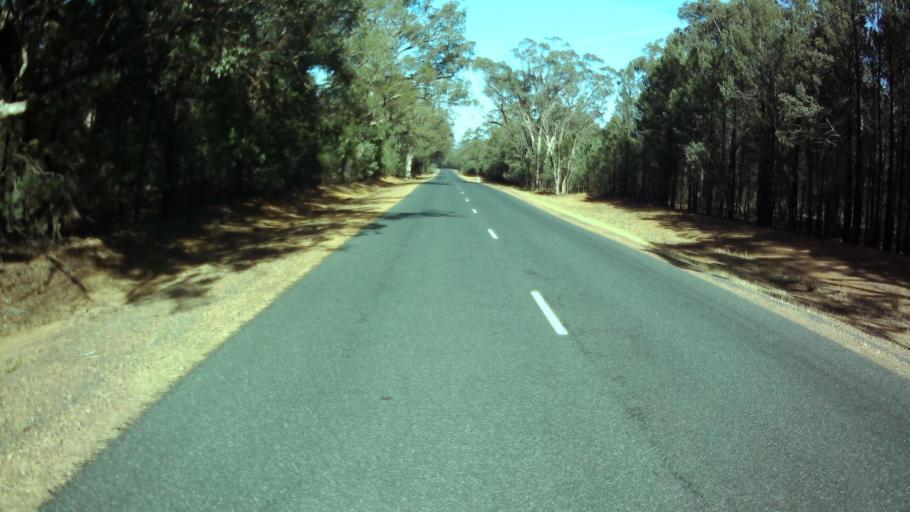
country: AU
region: New South Wales
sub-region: Weddin
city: Grenfell
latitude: -34.0254
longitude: 148.0421
